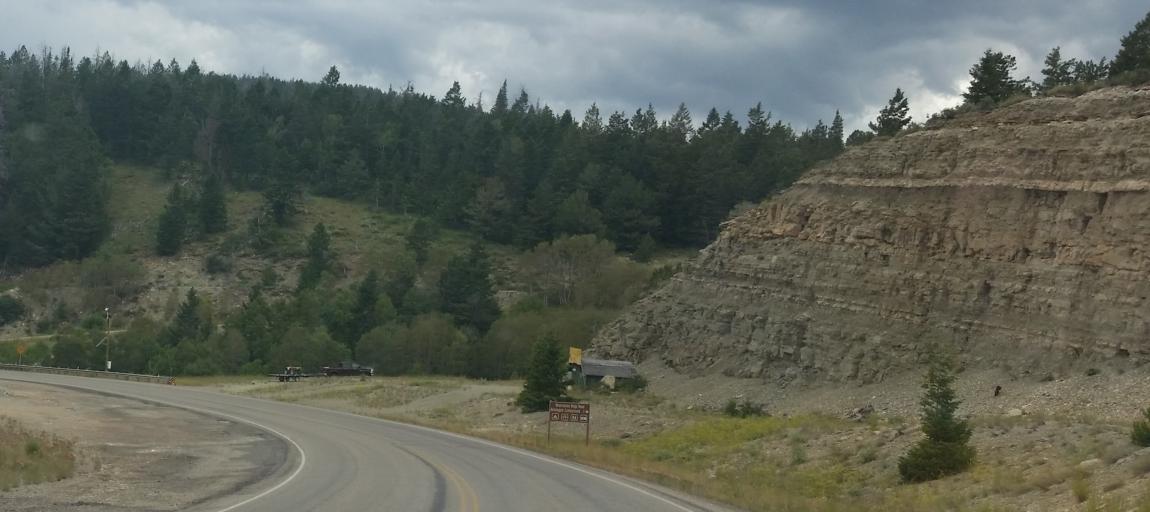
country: US
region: Utah
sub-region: Carbon County
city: Helper
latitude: 39.8794
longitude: -110.7581
